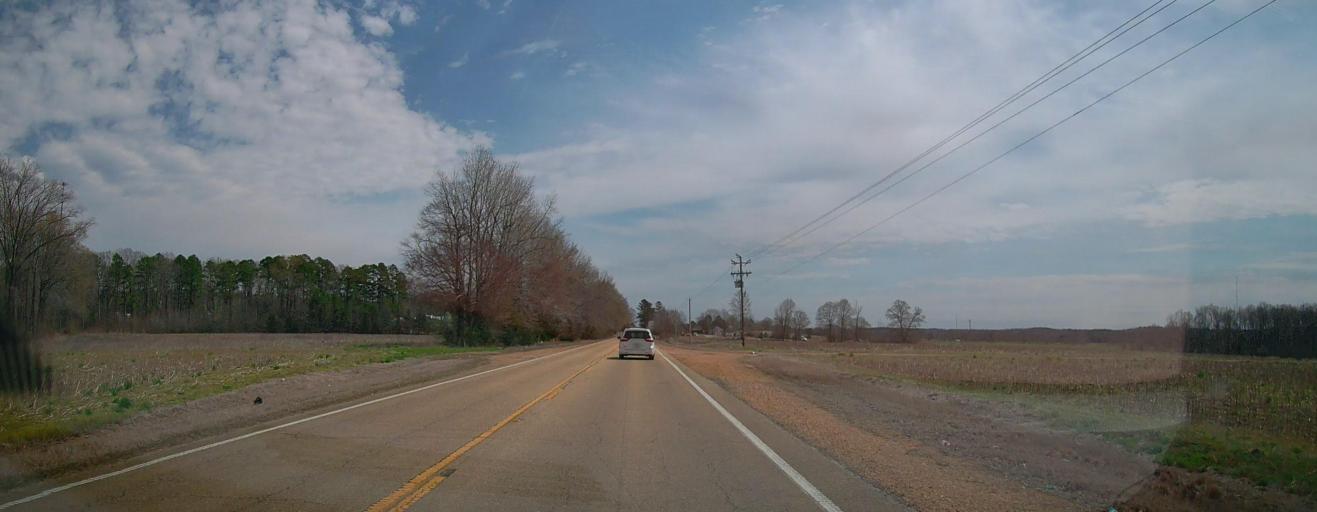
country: US
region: Mississippi
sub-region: Benton County
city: Ashland
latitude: 34.6190
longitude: -89.2199
